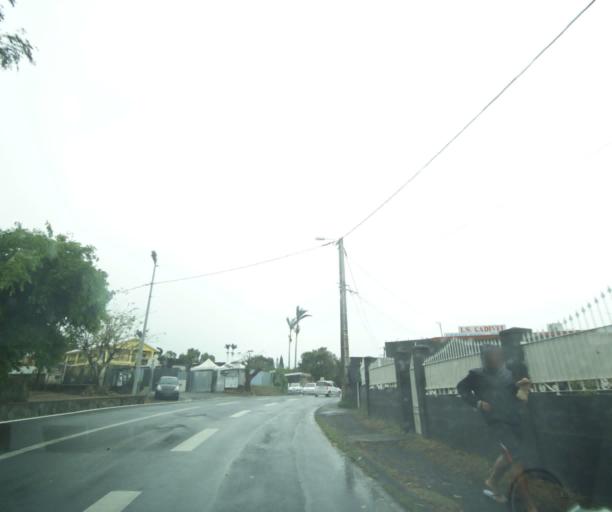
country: RE
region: Reunion
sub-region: Reunion
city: Saint-Paul
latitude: -21.0365
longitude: 55.2695
